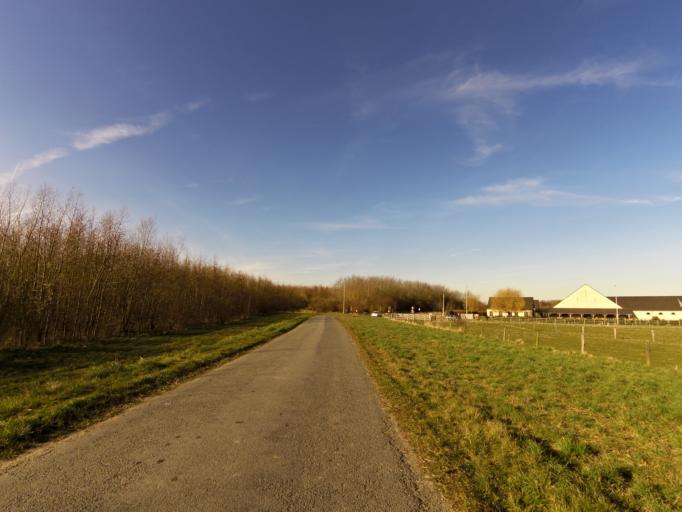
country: BE
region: Flanders
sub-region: Provincie West-Vlaanderen
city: Ostend
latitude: 51.1999
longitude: 2.9404
